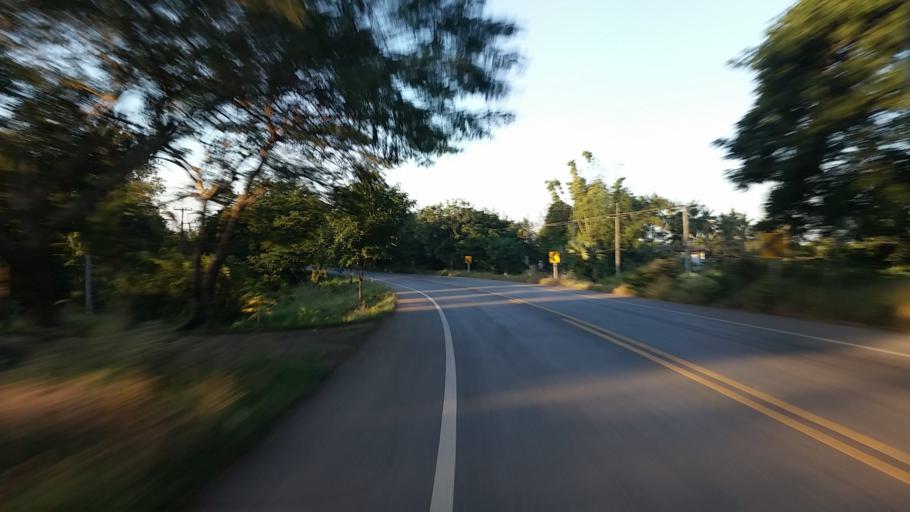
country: TH
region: Lop Buri
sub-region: Amphoe Lam Sonthi
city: Lam Sonthi
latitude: 15.2973
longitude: 101.3557
